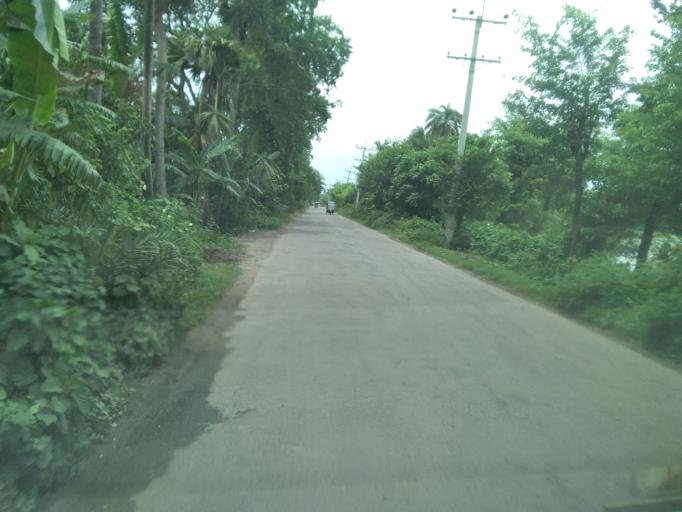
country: IN
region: West Bengal
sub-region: North 24 Parganas
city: Taki
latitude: 22.5704
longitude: 89.0010
